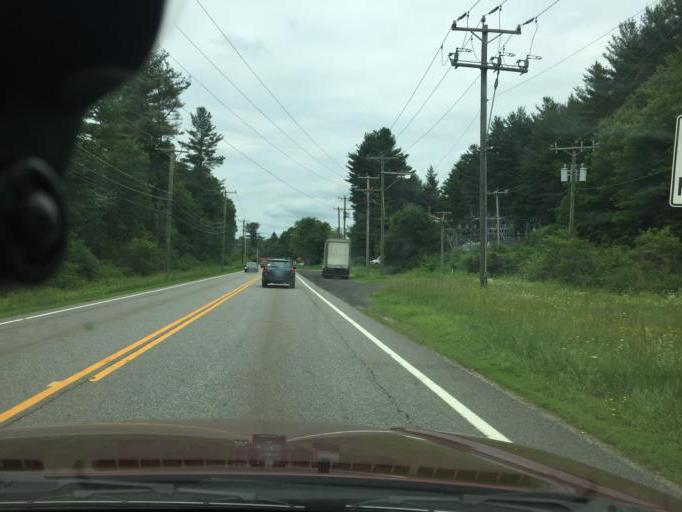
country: US
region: Connecticut
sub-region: Litchfield County
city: Litchfield
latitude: 41.7294
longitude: -73.2189
